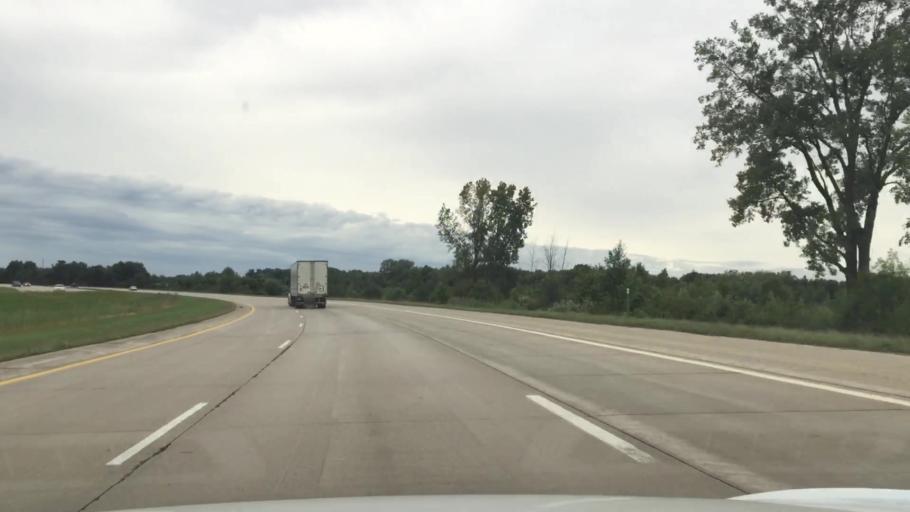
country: US
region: Michigan
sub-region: Saint Clair County
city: Marysville
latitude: 42.9491
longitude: -82.5069
